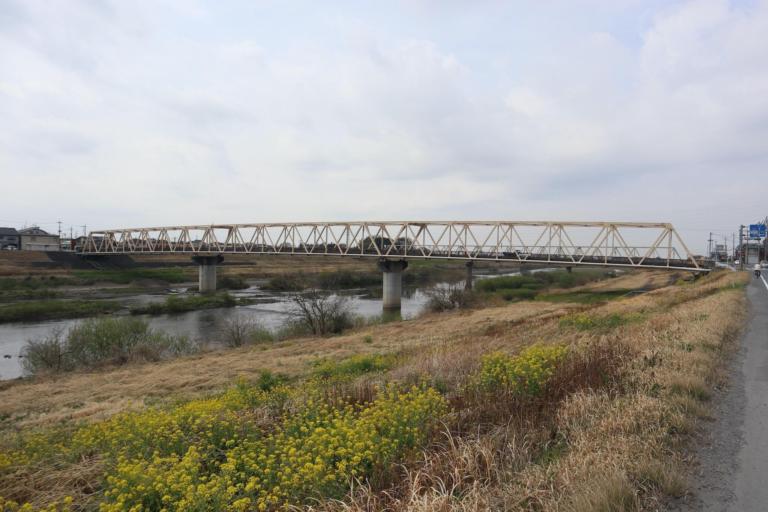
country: JP
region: Tochigi
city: Fujioka
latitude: 36.2656
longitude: 139.6513
